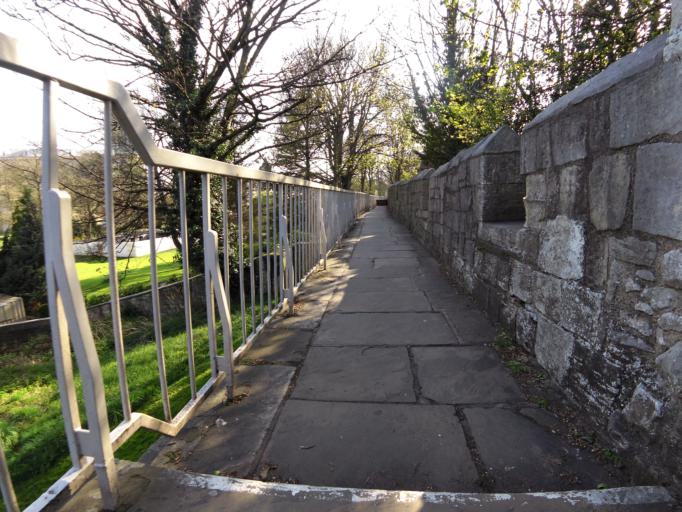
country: GB
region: England
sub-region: City of York
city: York
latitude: 53.9640
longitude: -1.0830
